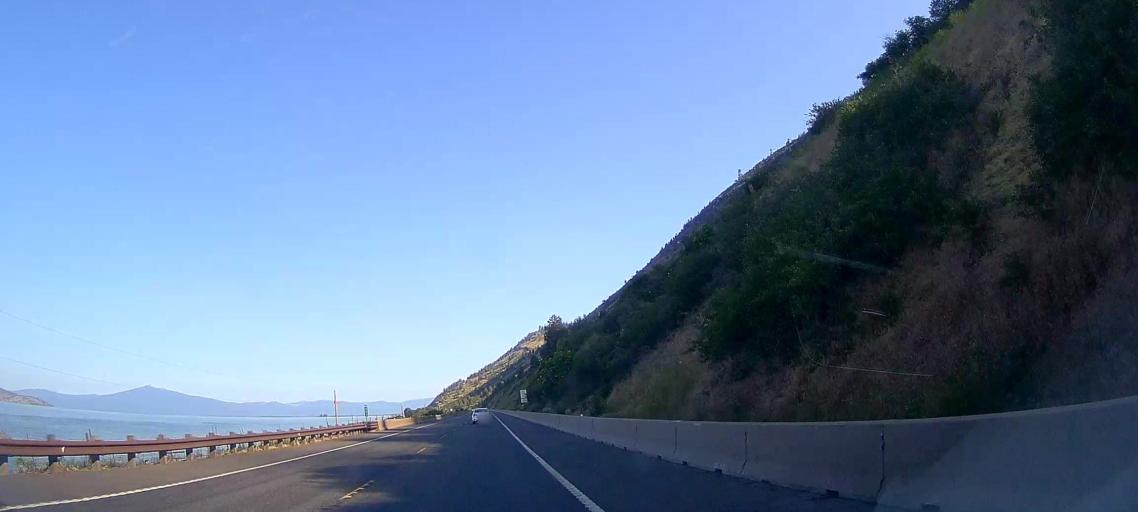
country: US
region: Oregon
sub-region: Klamath County
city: Klamath Falls
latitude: 42.4083
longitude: -121.8317
